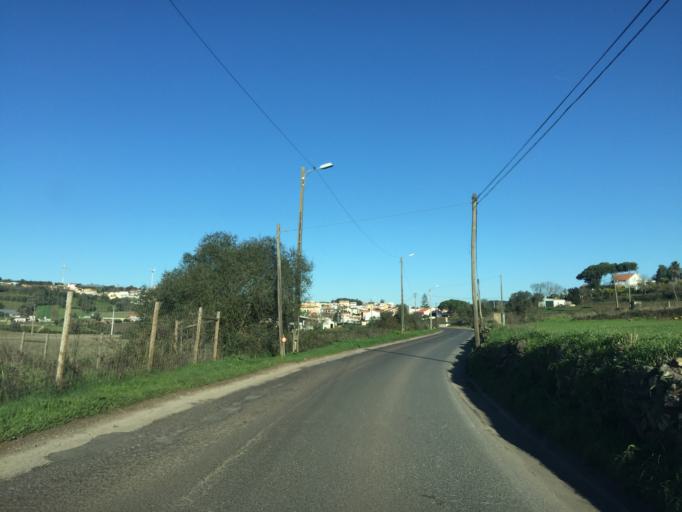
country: PT
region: Lisbon
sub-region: Odivelas
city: Canecas
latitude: 38.8296
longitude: -9.2491
